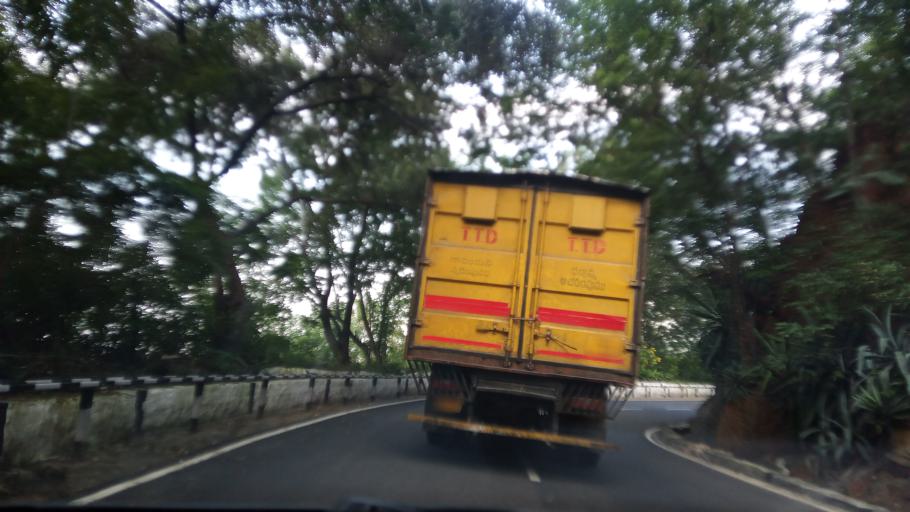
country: IN
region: Andhra Pradesh
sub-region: Chittoor
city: Tirumala
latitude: 13.6575
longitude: 79.3483
